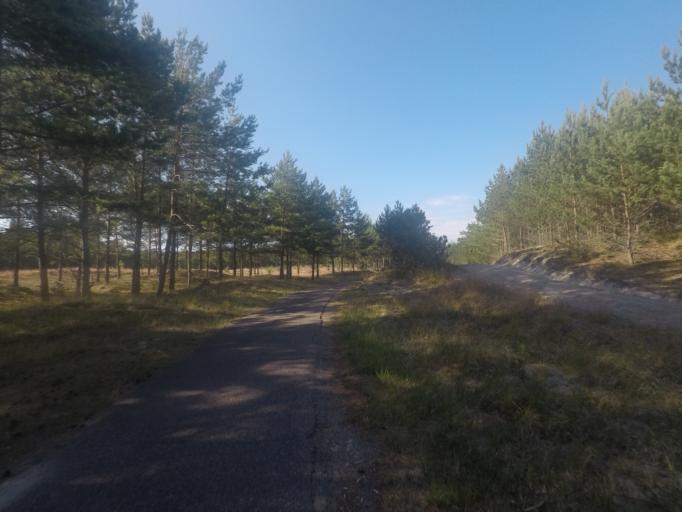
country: LT
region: Klaipedos apskritis
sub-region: Klaipeda
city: Klaipeda
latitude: 55.5734
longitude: 21.1135
